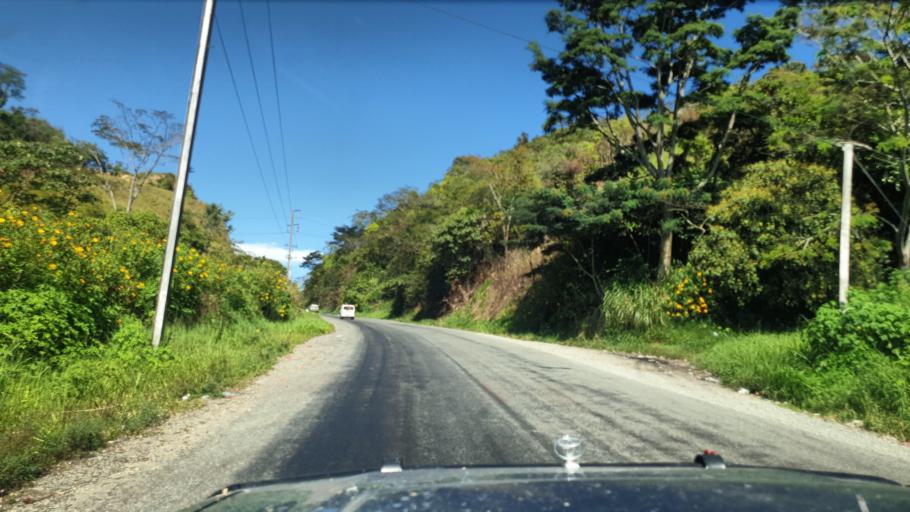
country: PG
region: Western Highlands
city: Rauna
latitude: -5.8257
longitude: 144.3749
